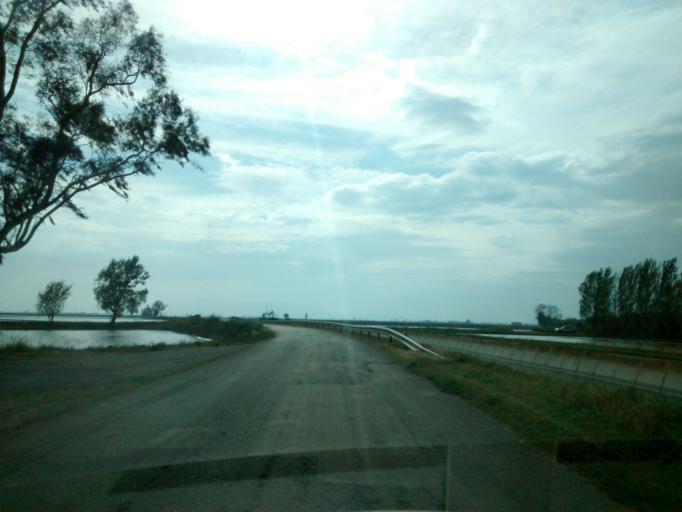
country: ES
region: Catalonia
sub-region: Provincia de Tarragona
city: Deltebre
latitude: 40.6927
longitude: 0.7926
